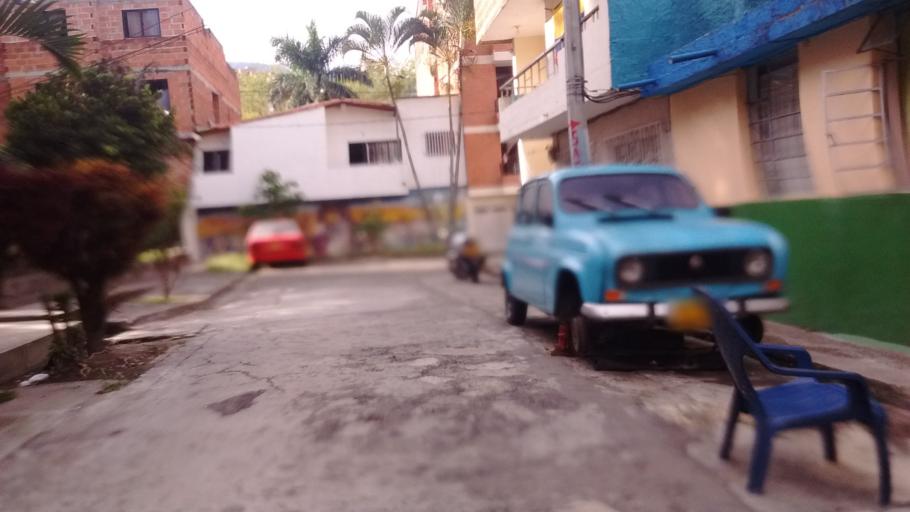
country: CO
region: Antioquia
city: Medellin
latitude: 6.2576
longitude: -75.6094
